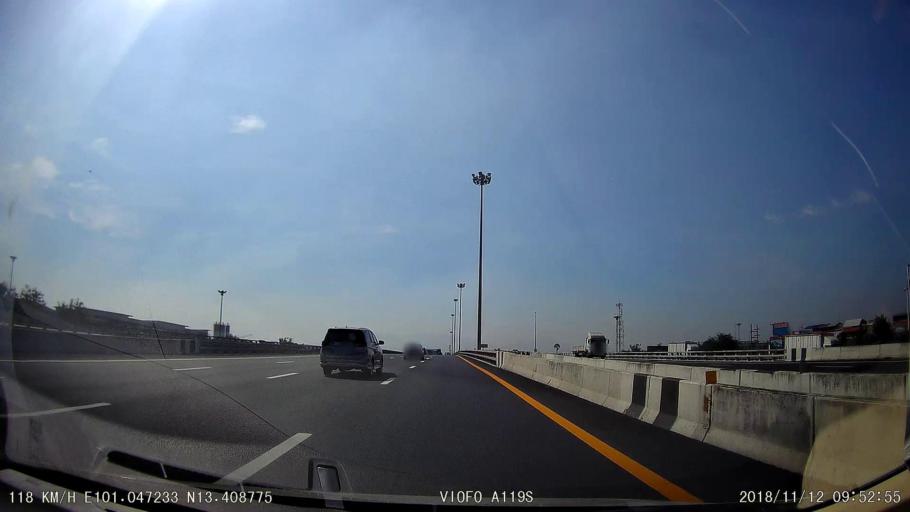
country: TH
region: Chon Buri
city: Phan Thong
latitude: 13.4073
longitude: 101.0471
